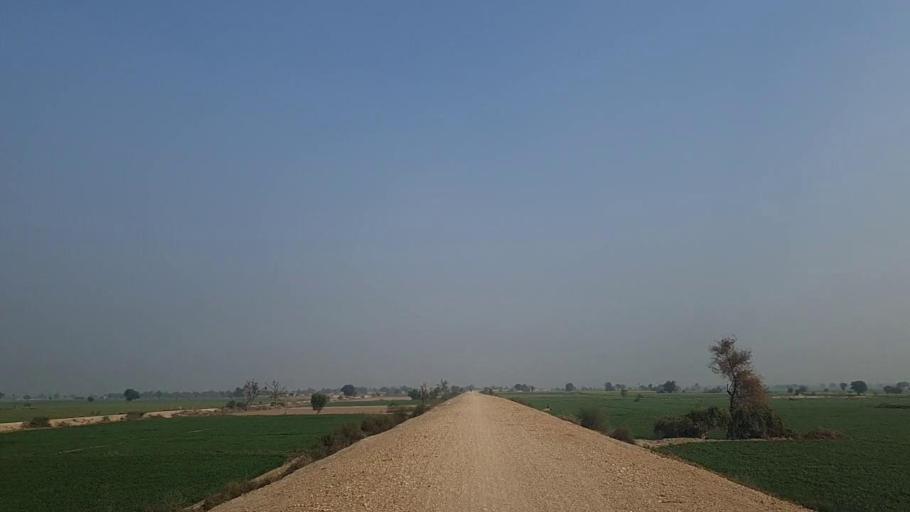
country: PK
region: Sindh
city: Sann
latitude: 26.0847
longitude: 68.1694
